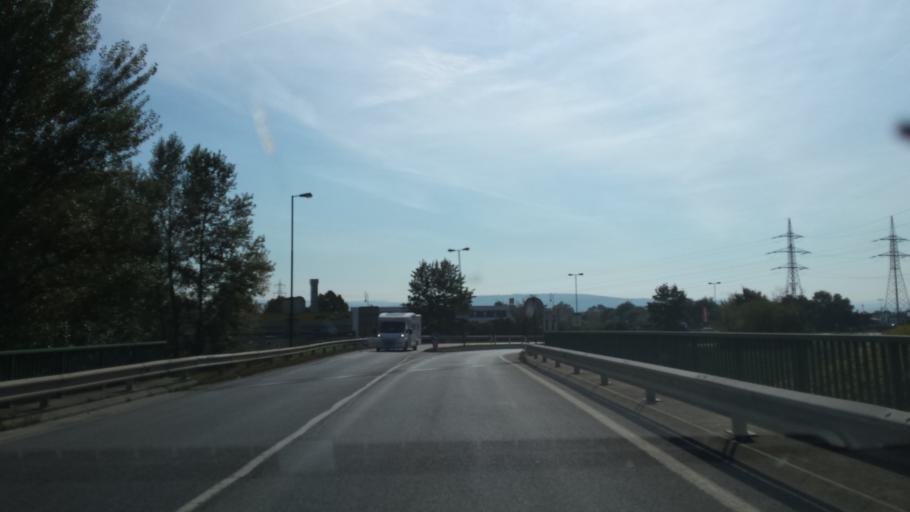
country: AT
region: Lower Austria
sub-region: Politischer Bezirk Tulln
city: Langenrohr
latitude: 48.3253
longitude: 16.0277
